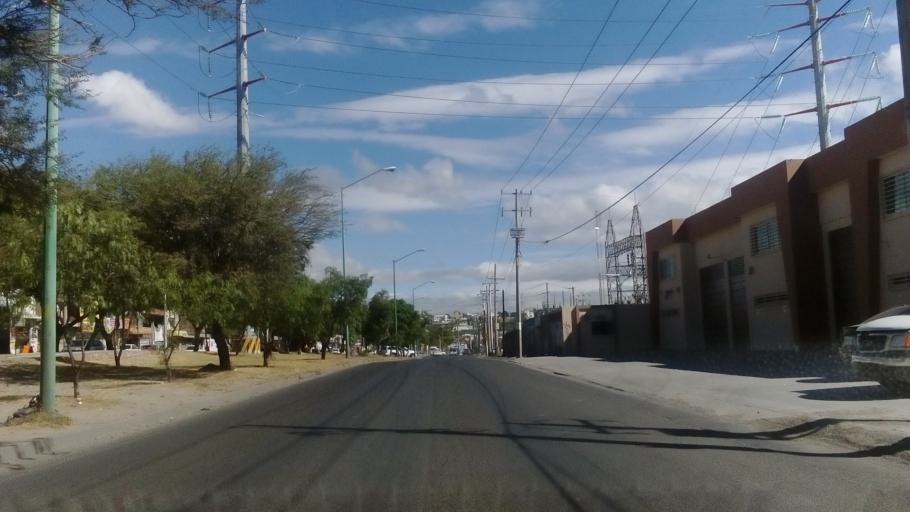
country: MX
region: Guanajuato
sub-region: Leon
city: Ejido la Joya
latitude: 21.1149
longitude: -101.7094
